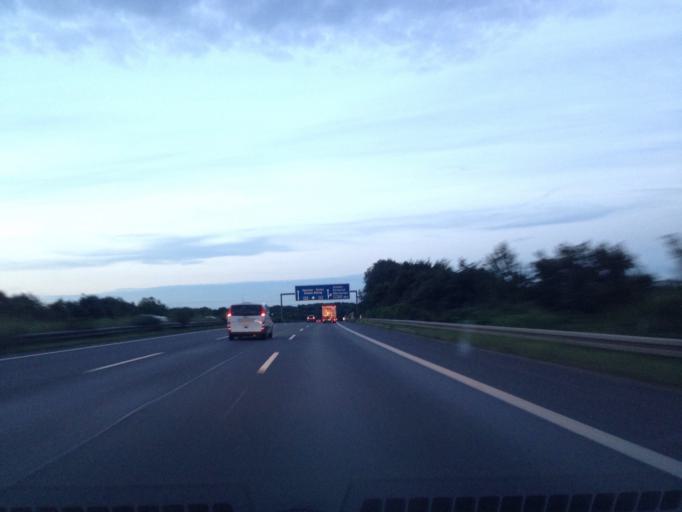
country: DE
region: North Rhine-Westphalia
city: Meiderich
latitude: 51.5271
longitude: 6.8174
